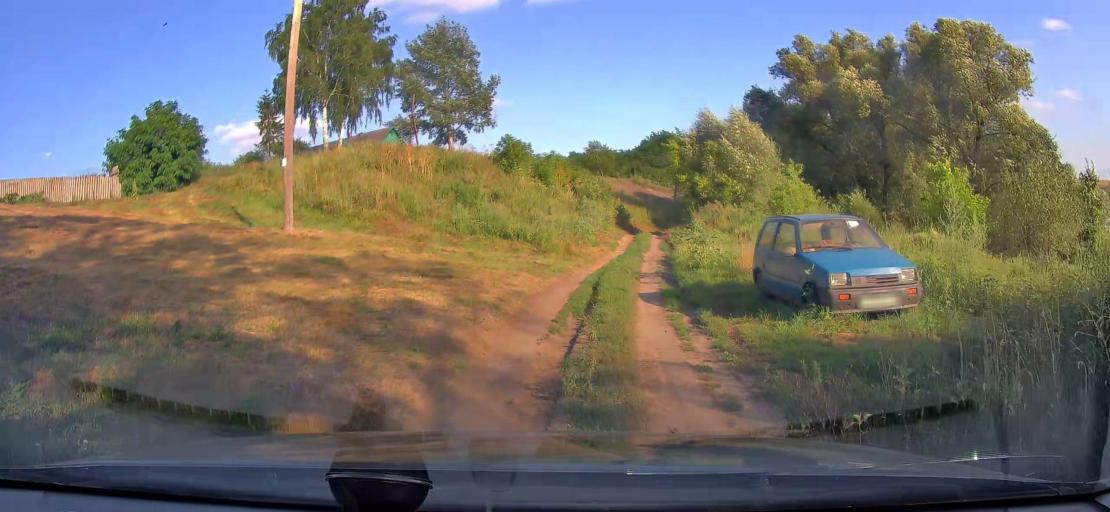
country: RU
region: Kursk
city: Zolotukhino
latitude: 52.0299
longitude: 36.2003
